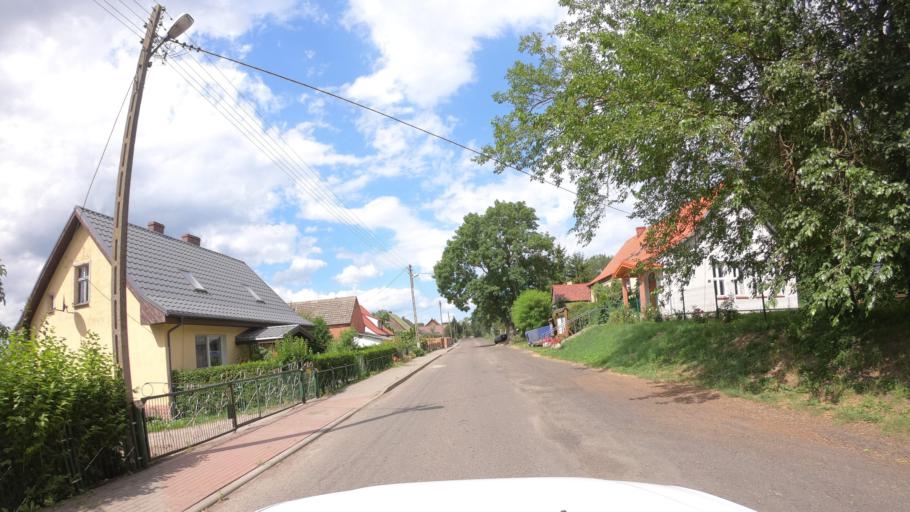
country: PL
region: West Pomeranian Voivodeship
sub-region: Powiat pyrzycki
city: Warnice
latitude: 53.2104
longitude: 14.9380
